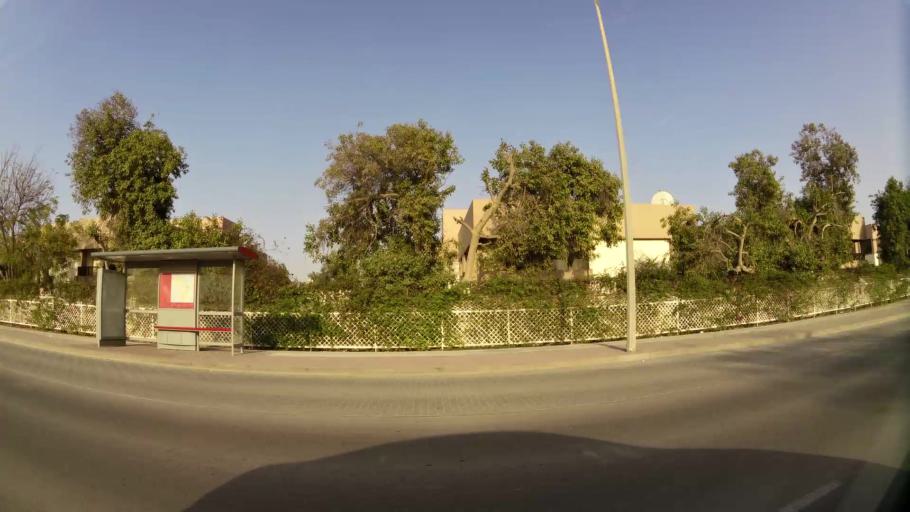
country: BH
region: Manama
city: Jidd Hafs
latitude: 26.2034
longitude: 50.4839
